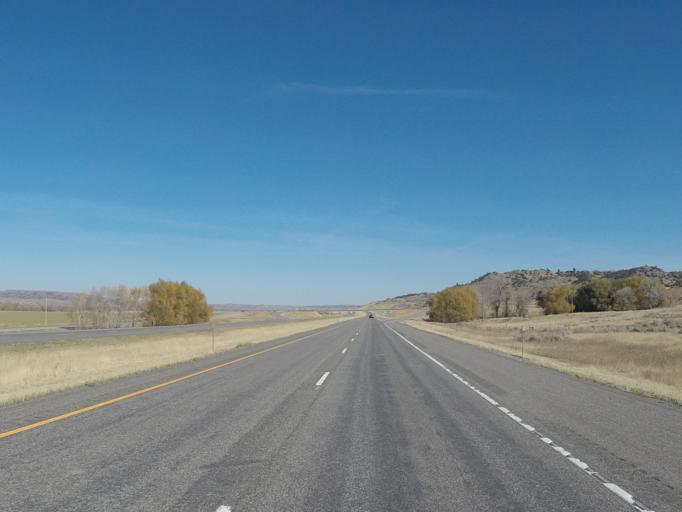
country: US
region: Montana
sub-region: Sweet Grass County
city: Big Timber
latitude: 45.7747
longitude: -110.0727
